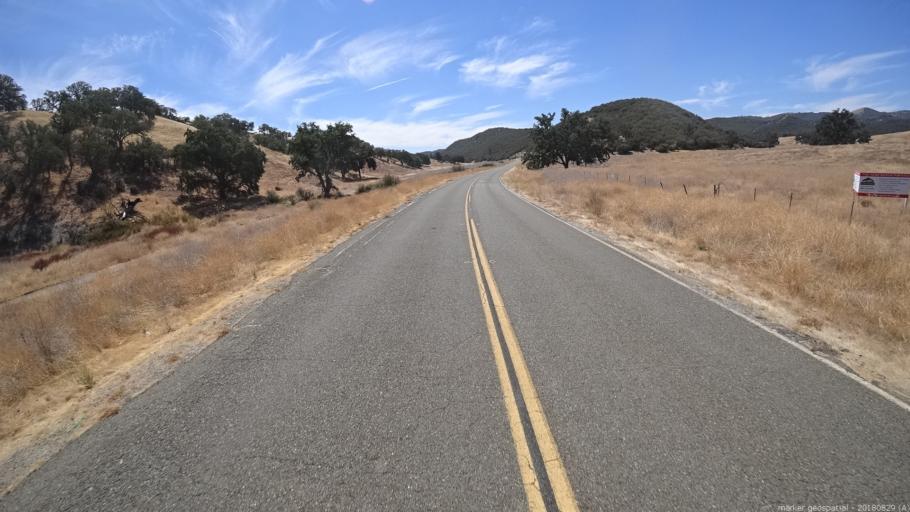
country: US
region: California
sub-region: San Luis Obispo County
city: Lake Nacimiento
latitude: 35.8833
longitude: -121.0655
